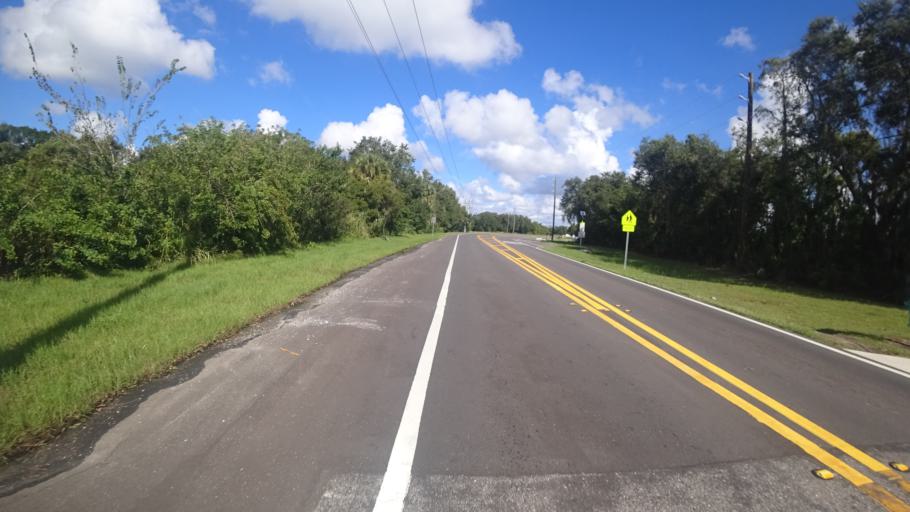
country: US
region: Florida
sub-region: Manatee County
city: Ellenton
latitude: 27.5689
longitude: -82.4789
